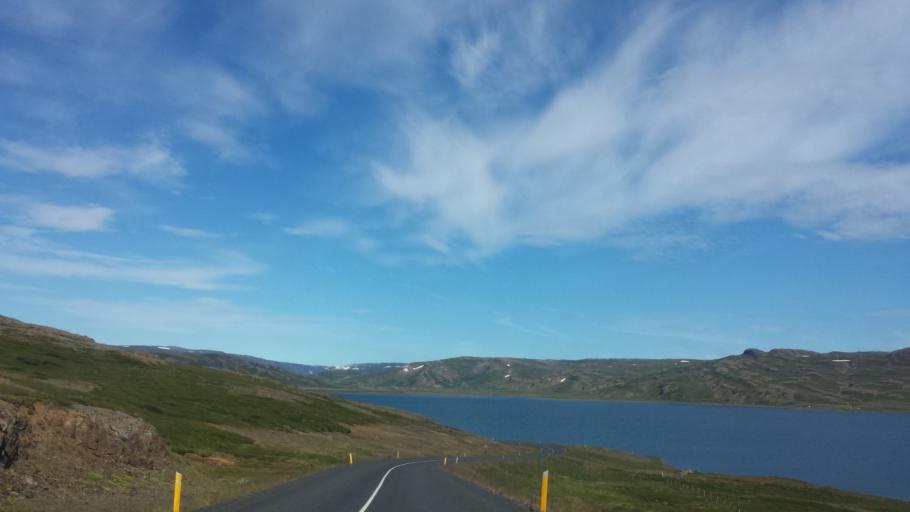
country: IS
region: West
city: Stykkisholmur
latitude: 65.7470
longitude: -21.7062
